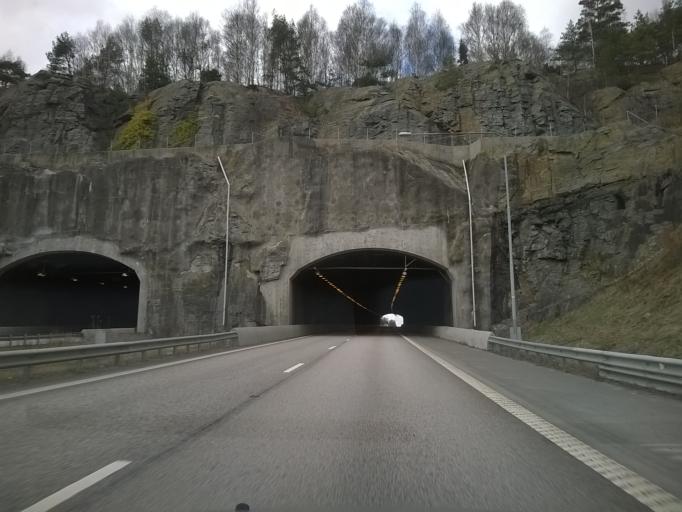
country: SE
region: Halland
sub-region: Varbergs Kommun
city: Veddige
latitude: 57.2351
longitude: 12.2240
